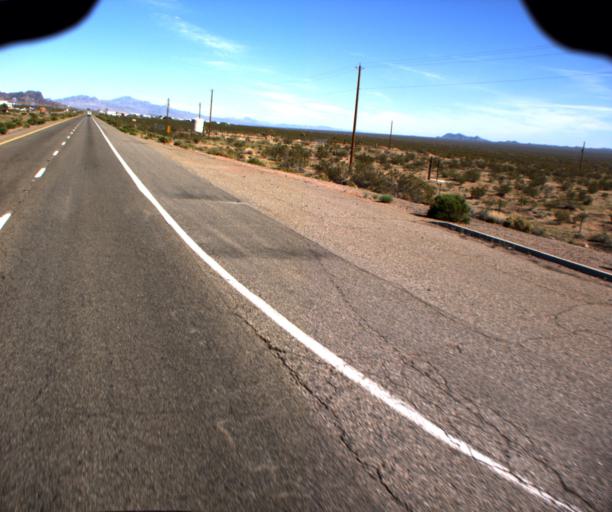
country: US
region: Arizona
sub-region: Mohave County
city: Dolan Springs
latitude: 35.7002
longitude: -114.4745
